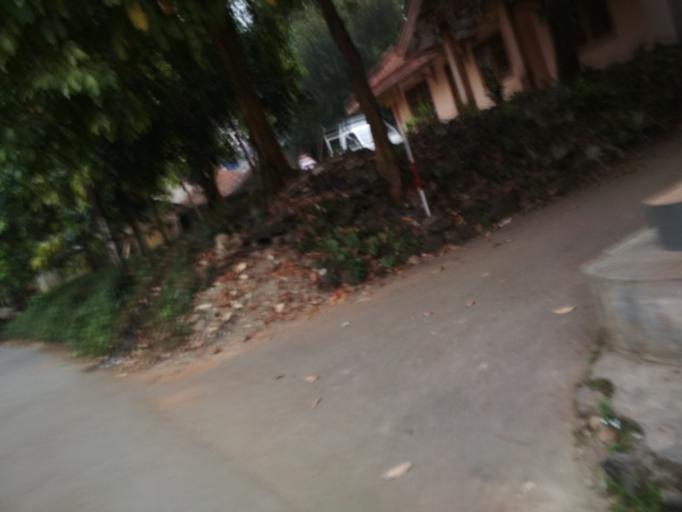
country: ID
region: West Java
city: Ciampea
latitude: -6.5588
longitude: 106.7382
